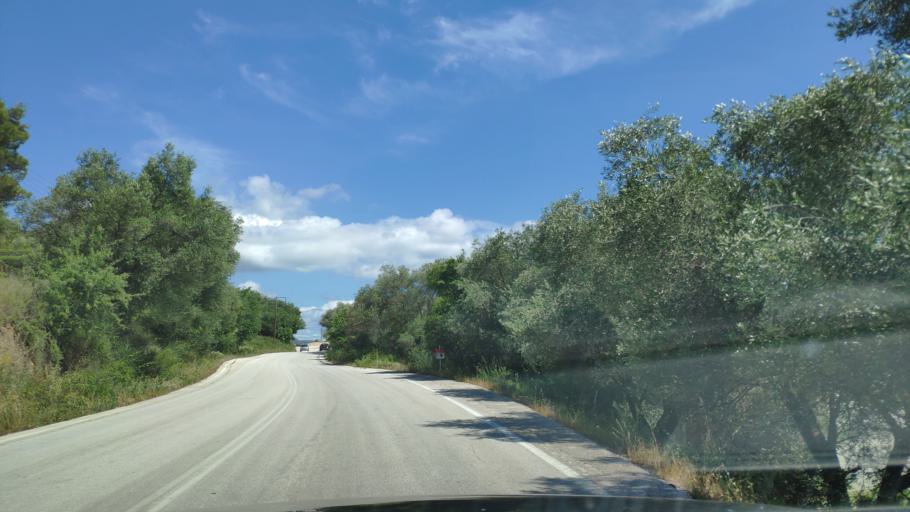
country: AL
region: Vlore
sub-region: Rrethi i Sarandes
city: Konispol
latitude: 39.6196
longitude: 20.2012
